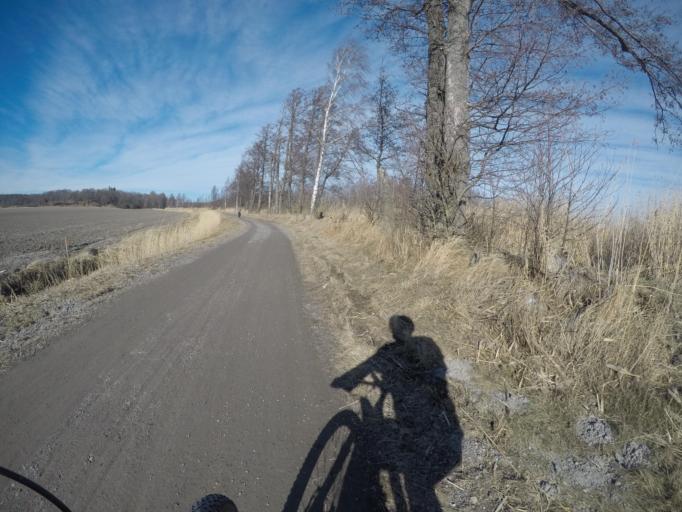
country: SE
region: Soedermanland
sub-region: Eskilstuna Kommun
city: Torshalla
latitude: 59.4054
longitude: 16.4654
